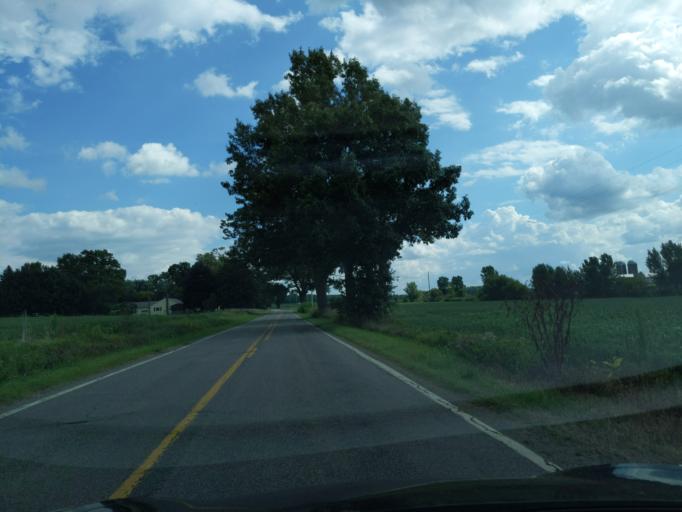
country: US
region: Michigan
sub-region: Jackson County
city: Spring Arbor
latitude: 42.3327
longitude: -84.5435
